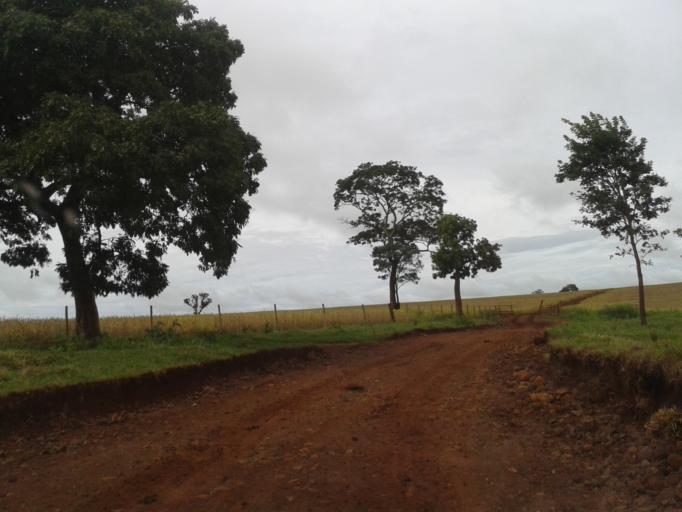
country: BR
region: Minas Gerais
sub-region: Capinopolis
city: Capinopolis
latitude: -18.7404
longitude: -49.7734
